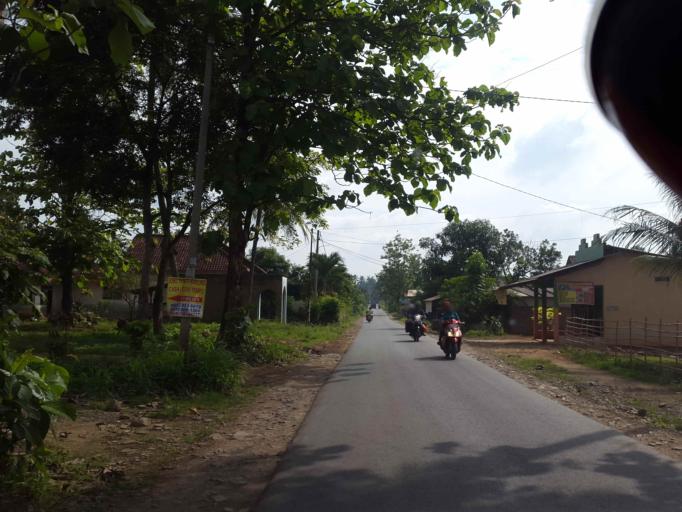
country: ID
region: Lampung
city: Natar
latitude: -5.3111
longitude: 105.1999
